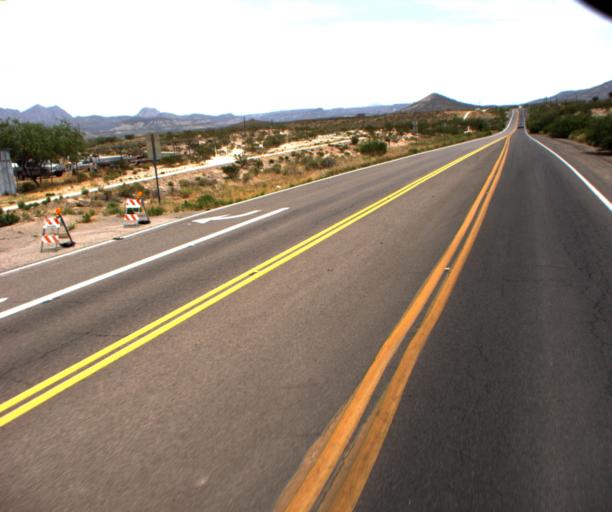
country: US
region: Arizona
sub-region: Gila County
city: Peridot
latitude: 33.2927
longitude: -110.4354
